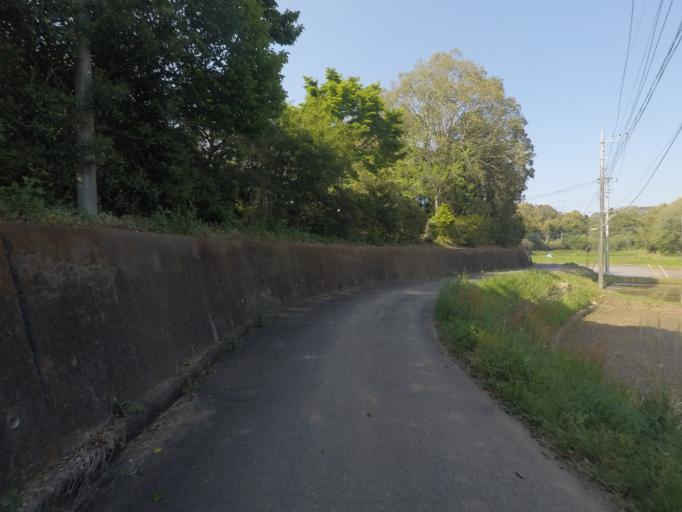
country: JP
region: Ibaraki
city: Itako
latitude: 36.0514
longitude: 140.4495
